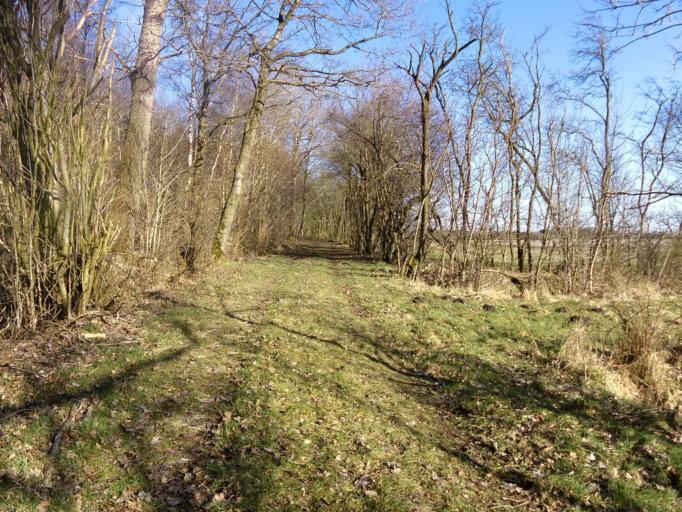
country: DK
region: South Denmark
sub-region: Haderslev Kommune
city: Gram
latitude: 55.2616
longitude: 8.9453
